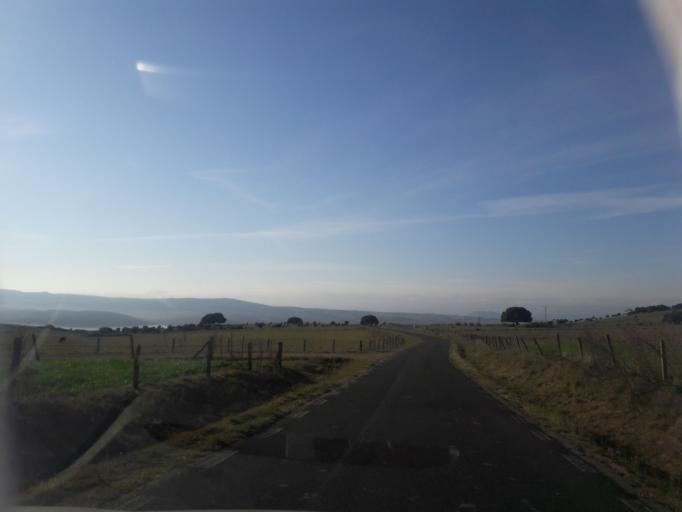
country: ES
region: Castille and Leon
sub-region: Provincia de Salamanca
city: Salvatierra de Tormes
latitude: 40.6111
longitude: -5.6031
